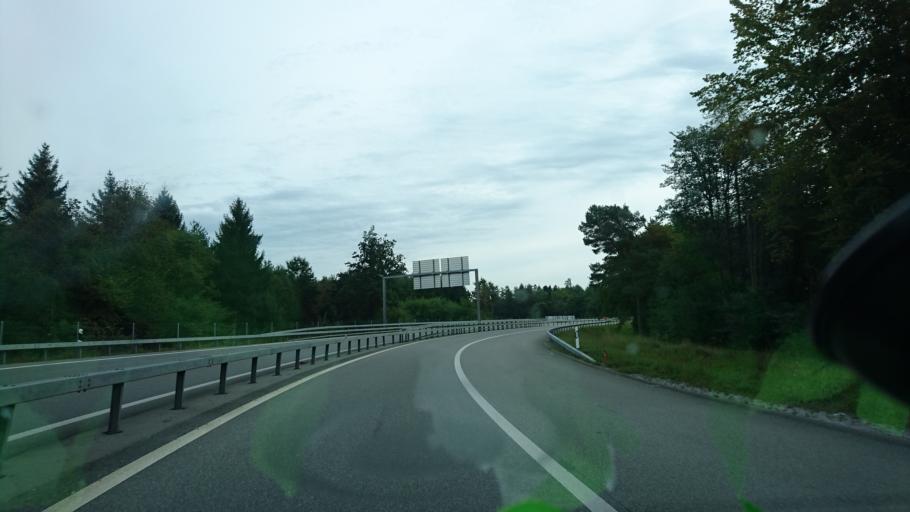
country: CH
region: Bern
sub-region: Bern-Mittelland District
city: Koniz
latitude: 46.9545
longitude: 7.4138
